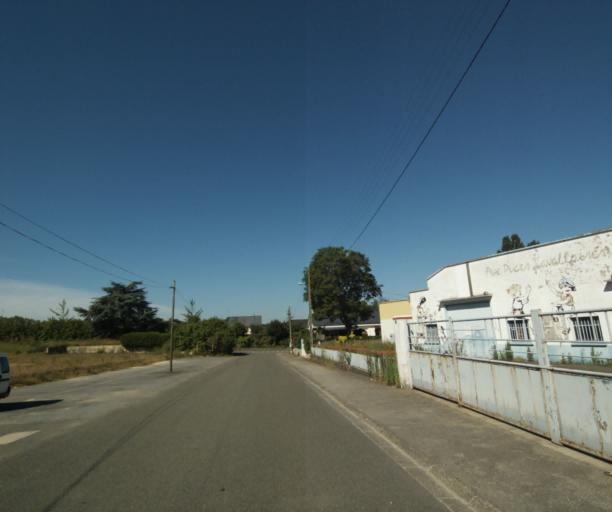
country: FR
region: Pays de la Loire
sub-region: Departement de la Mayenne
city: Laval
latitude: 48.0564
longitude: -0.7498
